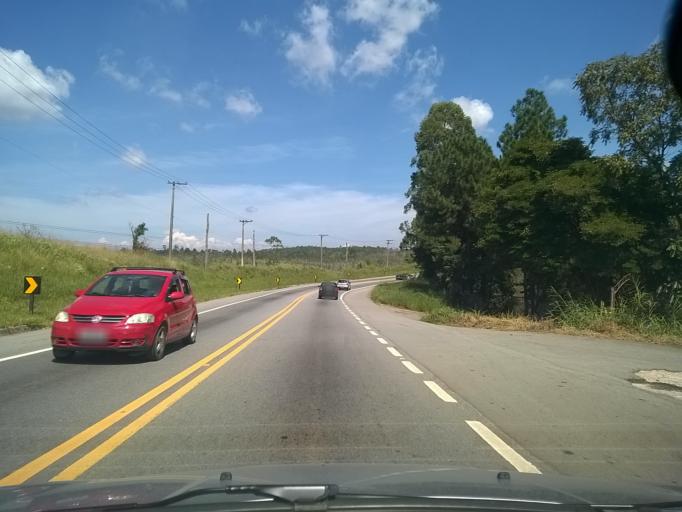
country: BR
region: Sao Paulo
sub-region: Francisco Morato
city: Francisco Morato
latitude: -23.2964
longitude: -46.7699
